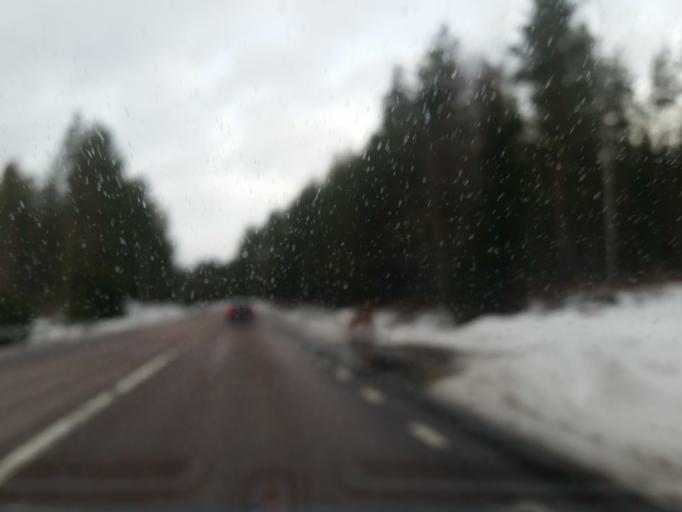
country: SE
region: Gaevleborg
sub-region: Sandvikens Kommun
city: Jarbo
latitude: 60.6936
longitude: 16.6353
